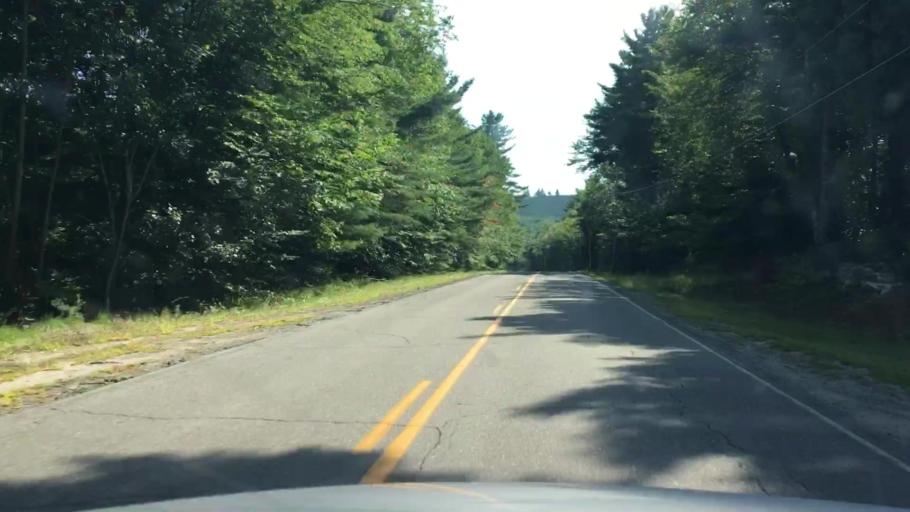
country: US
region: Maine
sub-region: Penobscot County
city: Enfield
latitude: 45.2986
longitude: -68.5522
